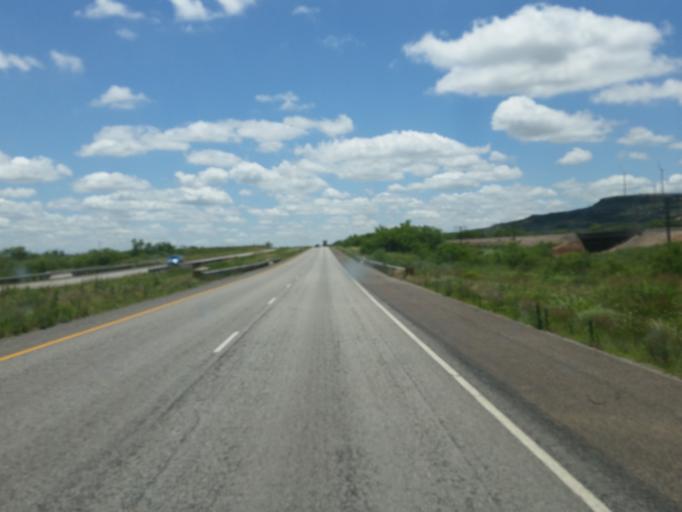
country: US
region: Texas
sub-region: Scurry County
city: Snyder
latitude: 32.9728
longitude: -101.1003
